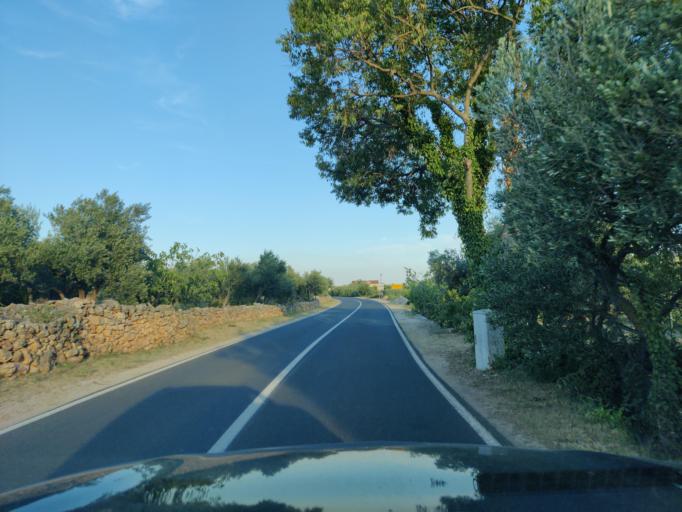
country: HR
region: Sibensko-Kniniska
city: Tribunj
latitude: 43.7690
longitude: 15.7292
